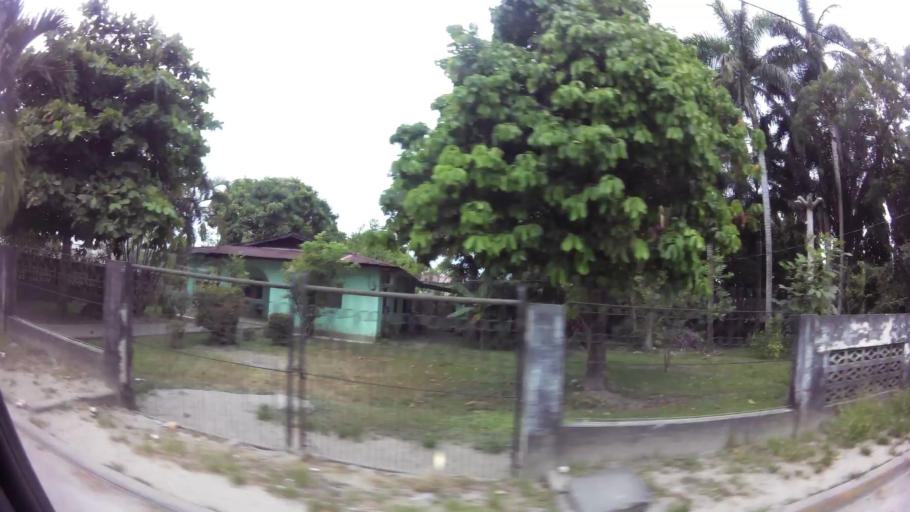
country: HN
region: Atlantida
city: Tela
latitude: 15.7634
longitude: -87.4799
